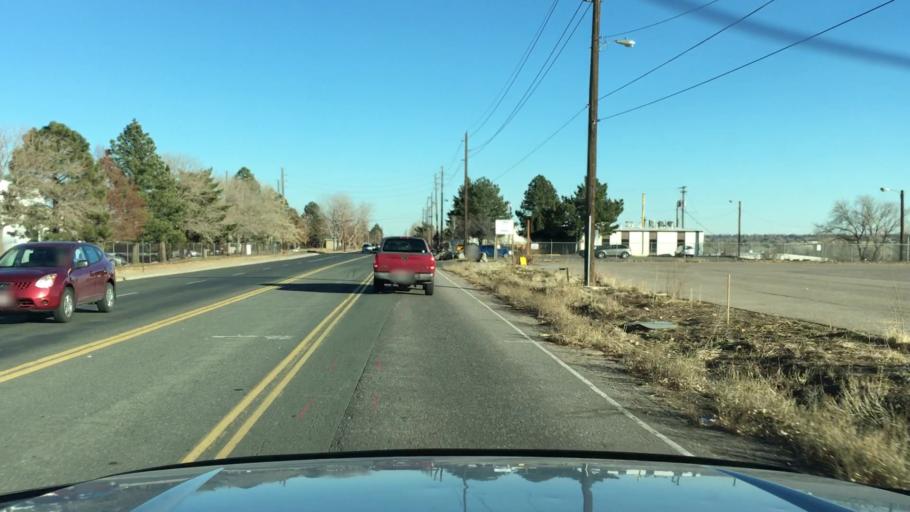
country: US
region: Colorado
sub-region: Jefferson County
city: Applewood
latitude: 39.7761
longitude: -105.1673
